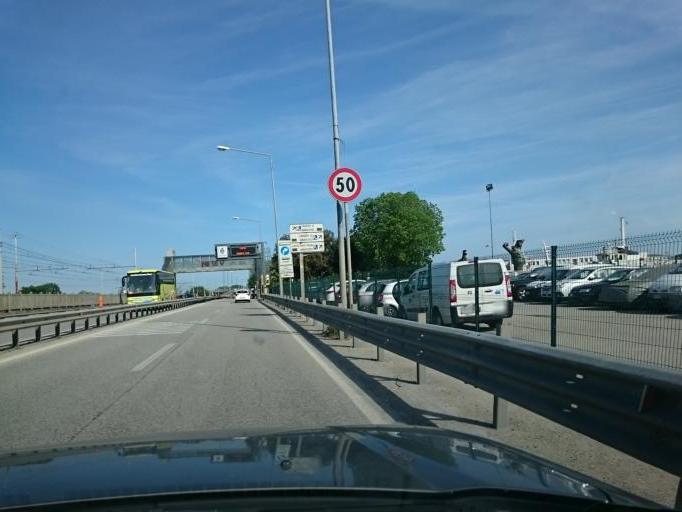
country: IT
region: Veneto
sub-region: Provincia di Venezia
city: Mestre
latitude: 45.4701
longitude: 12.2621
